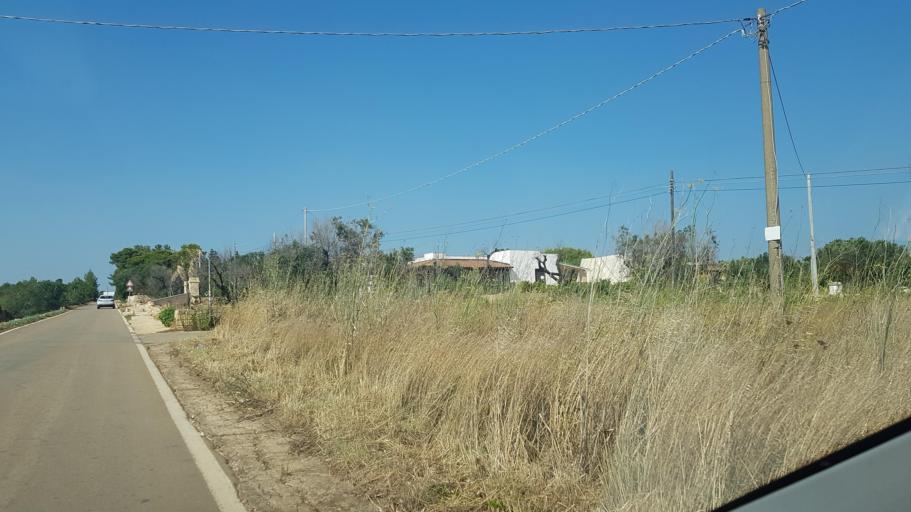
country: IT
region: Apulia
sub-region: Provincia di Lecce
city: Gemini
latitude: 39.8473
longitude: 18.2074
